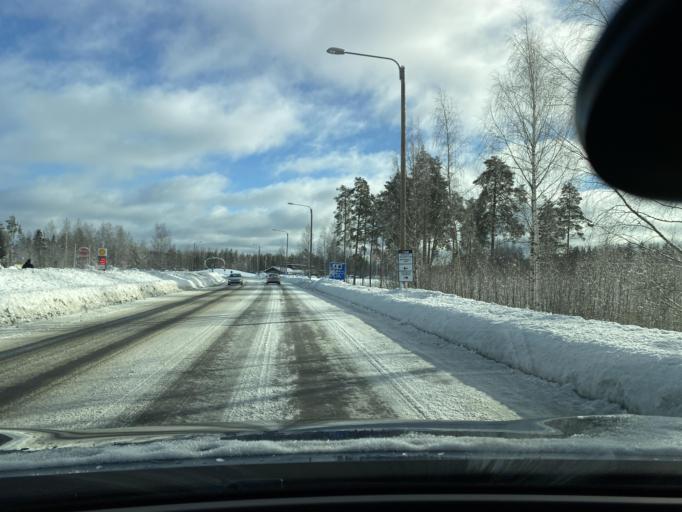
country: FI
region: Southern Savonia
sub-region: Mikkeli
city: Kangasniemi
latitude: 62.0037
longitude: 26.6532
